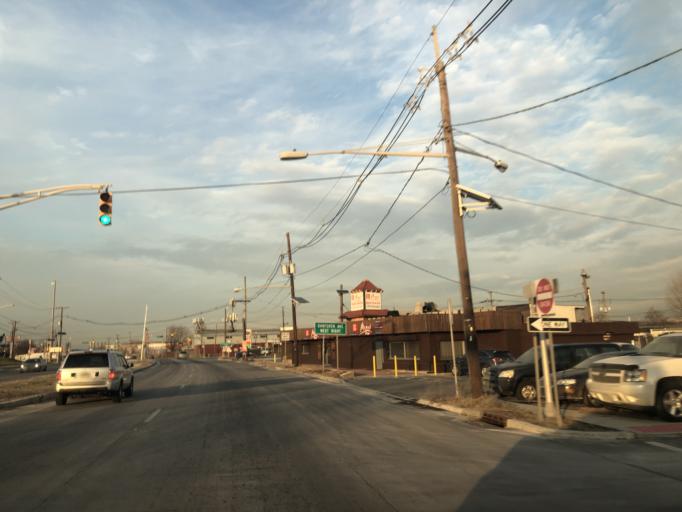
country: US
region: New Jersey
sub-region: Hudson County
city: Jersey City
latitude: 40.7048
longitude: -74.1000
